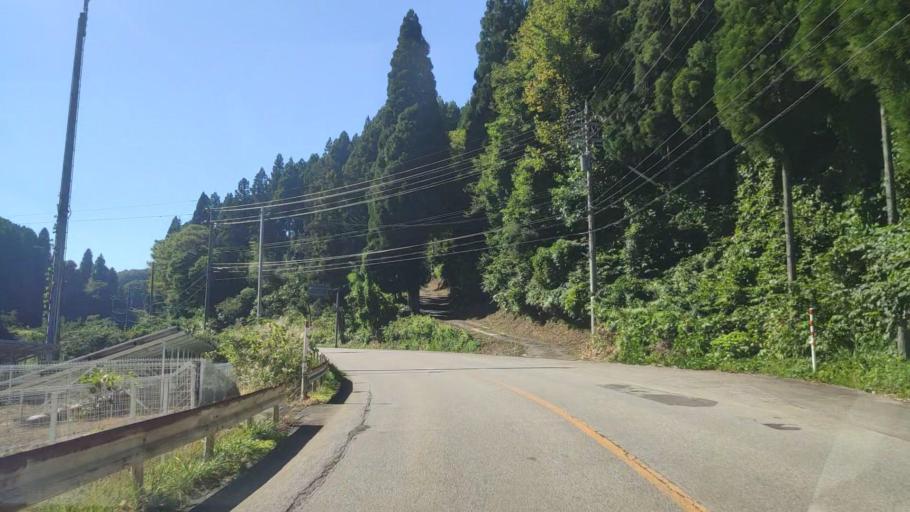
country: JP
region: Ishikawa
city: Nanao
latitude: 37.3217
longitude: 137.1837
